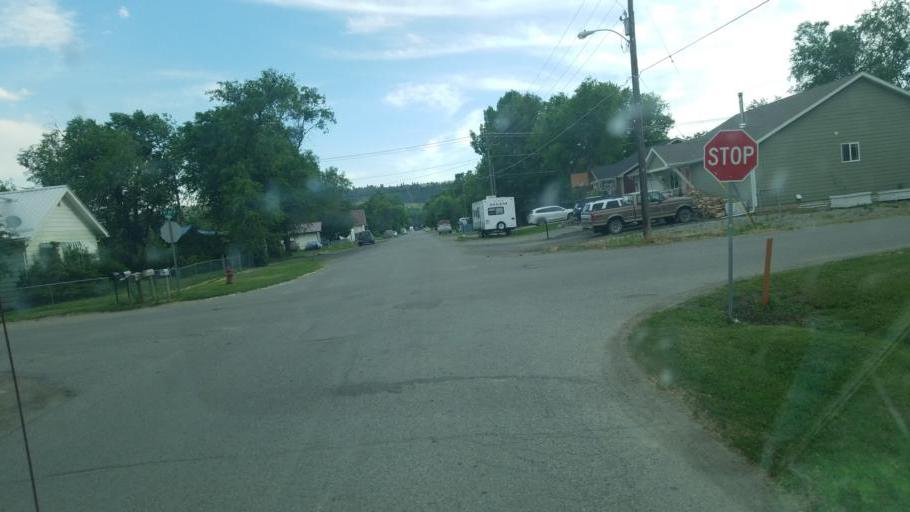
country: US
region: Montana
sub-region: Stillwater County
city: Columbus
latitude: 45.6406
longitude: -109.2492
